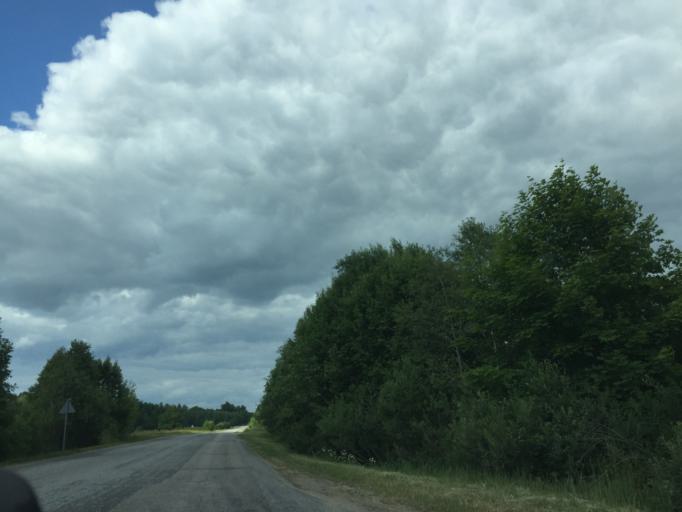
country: LV
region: Skriveri
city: Skriveri
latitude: 56.8226
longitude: 25.1217
